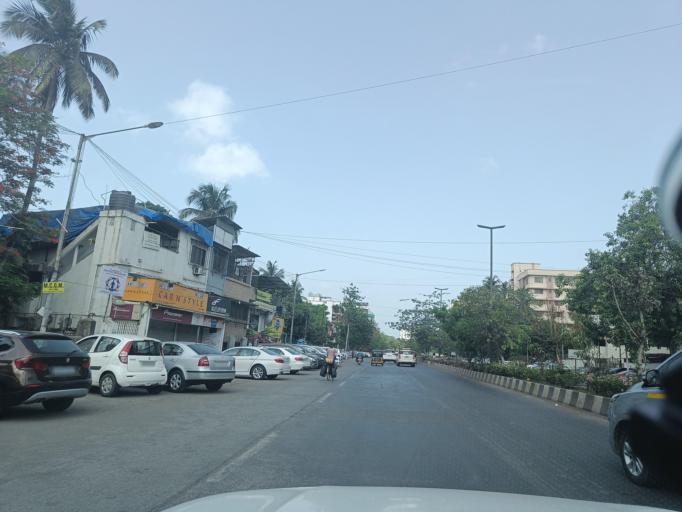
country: IN
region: Maharashtra
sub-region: Mumbai Suburban
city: Powai
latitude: 19.1115
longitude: 72.8657
